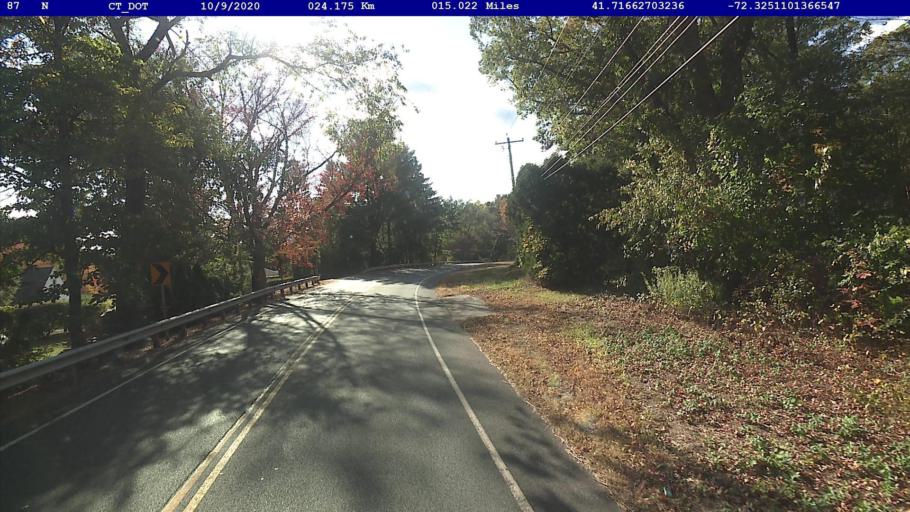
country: US
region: Connecticut
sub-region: Tolland County
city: Coventry Lake
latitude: 41.7170
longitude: -72.3255
